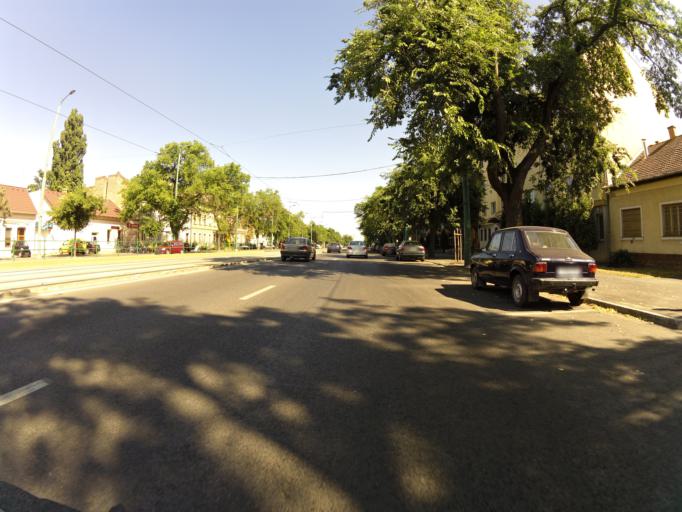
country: HU
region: Csongrad
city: Szeged
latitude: 46.2625
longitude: 20.1356
